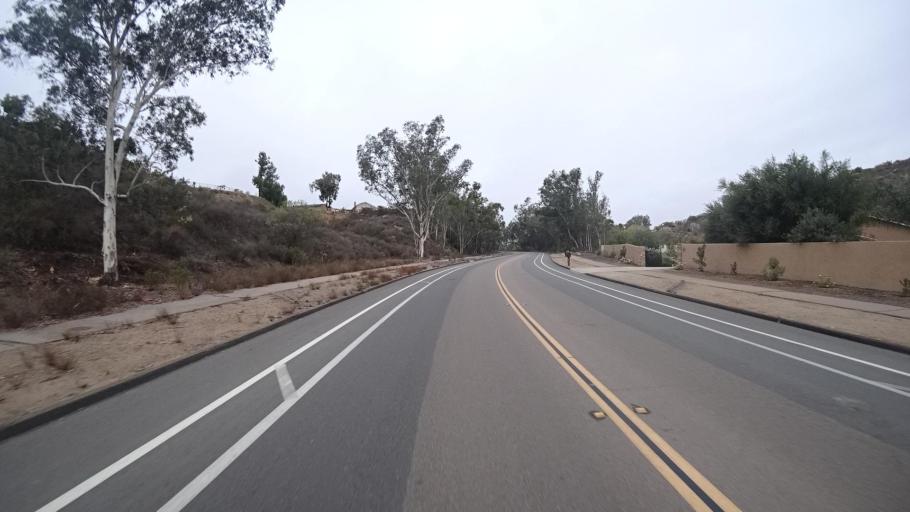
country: US
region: California
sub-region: San Diego County
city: Rancho San Diego
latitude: 32.7596
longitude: -116.9063
